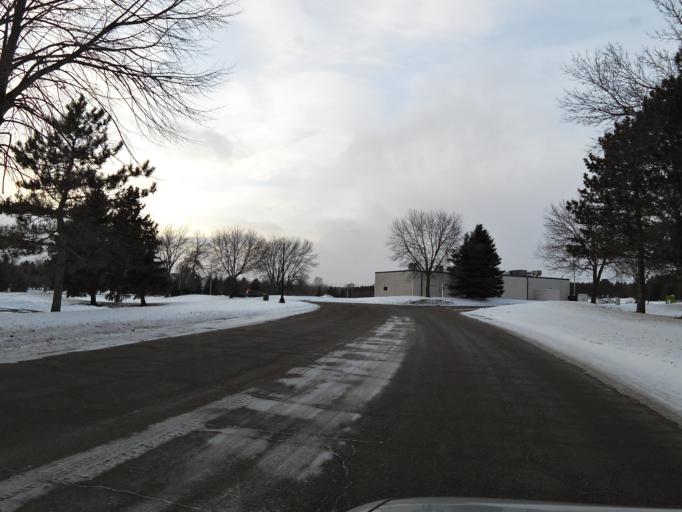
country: US
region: Minnesota
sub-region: Washington County
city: Lake Elmo
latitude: 44.9625
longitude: -92.8814
